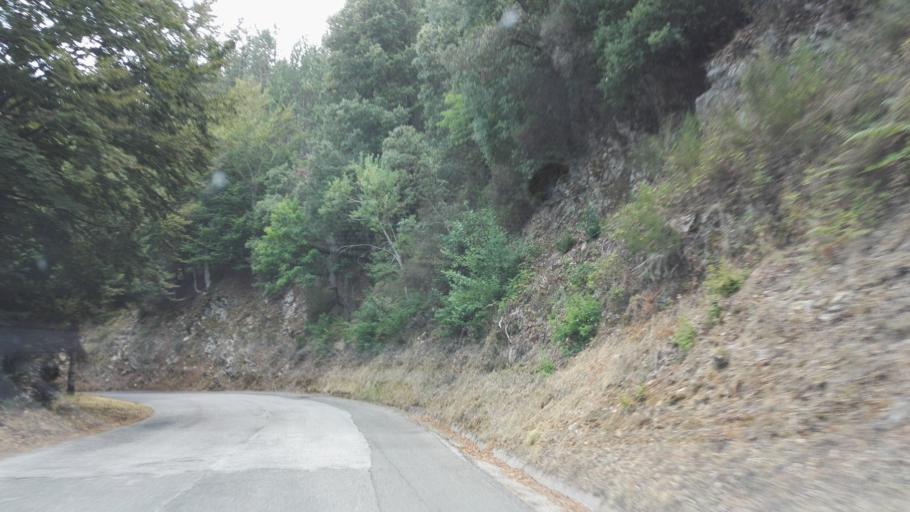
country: IT
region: Calabria
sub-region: Provincia di Vibo-Valentia
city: Nardodipace
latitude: 38.4846
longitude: 16.3432
